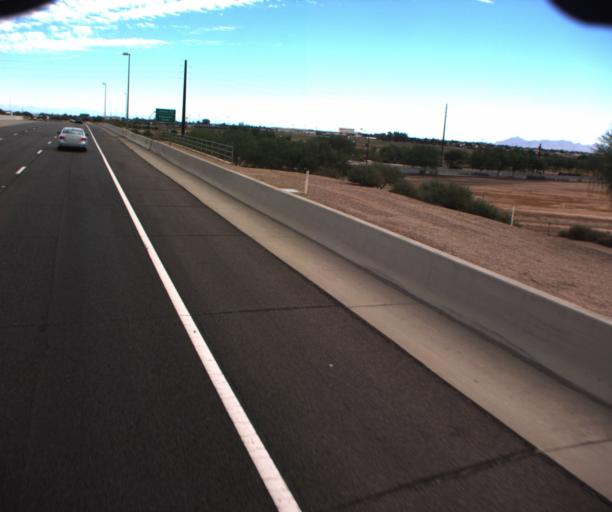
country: US
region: Arizona
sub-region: Maricopa County
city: Chandler
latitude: 33.2830
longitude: -111.7749
